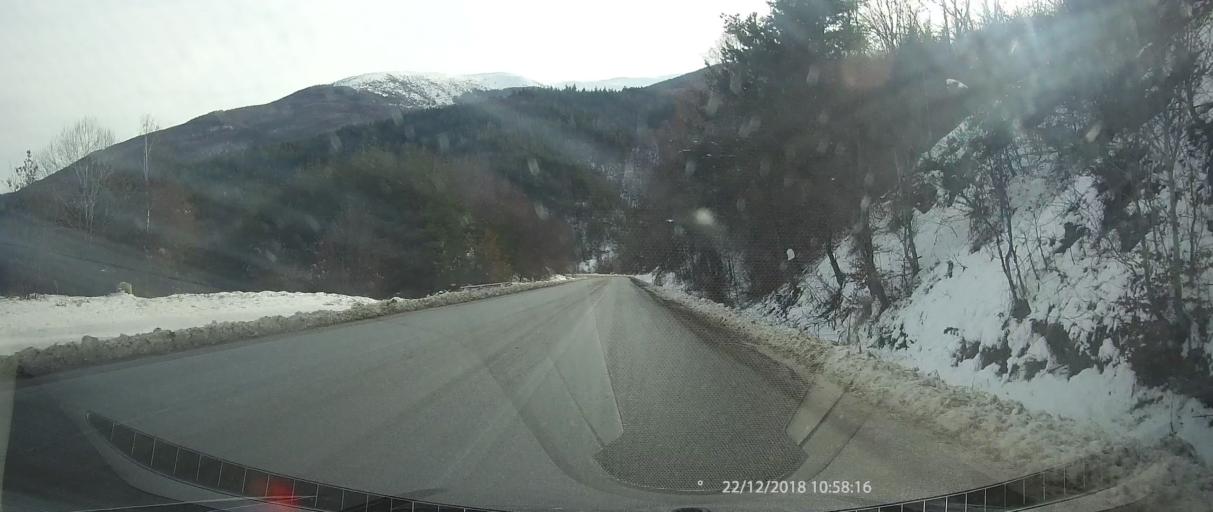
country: MK
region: Kriva Palanka
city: Kriva Palanka
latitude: 42.2180
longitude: 22.4676
